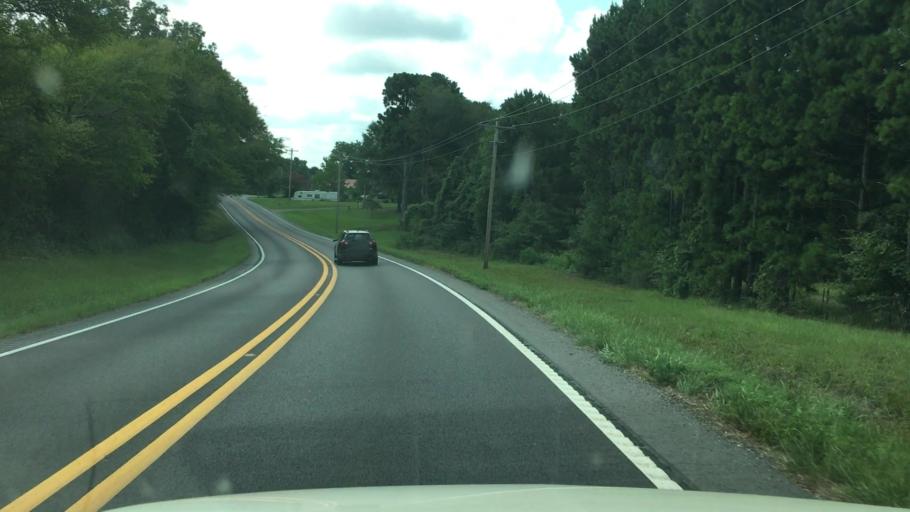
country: US
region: Arkansas
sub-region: Garland County
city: Lake Hamilton
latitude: 34.3032
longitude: -93.1663
